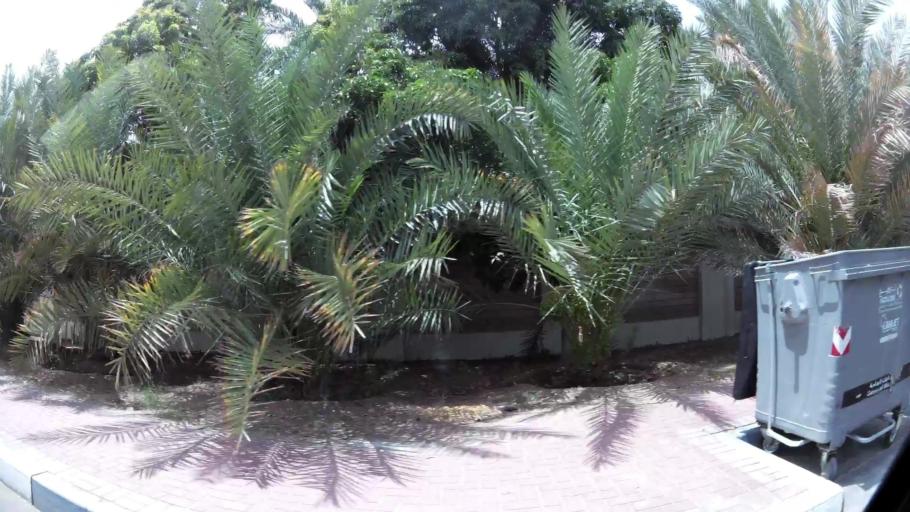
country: AE
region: Abu Dhabi
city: Al Ain
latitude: 24.1878
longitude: 55.6759
